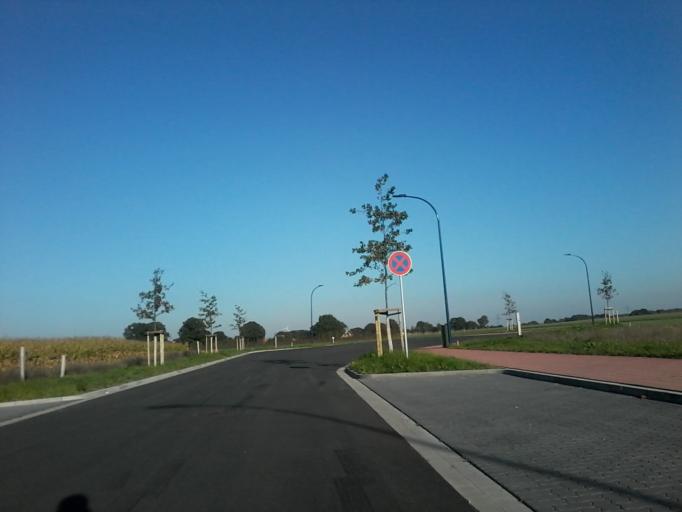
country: DE
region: Lower Saxony
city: Oyten
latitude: 53.0510
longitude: 9.0432
